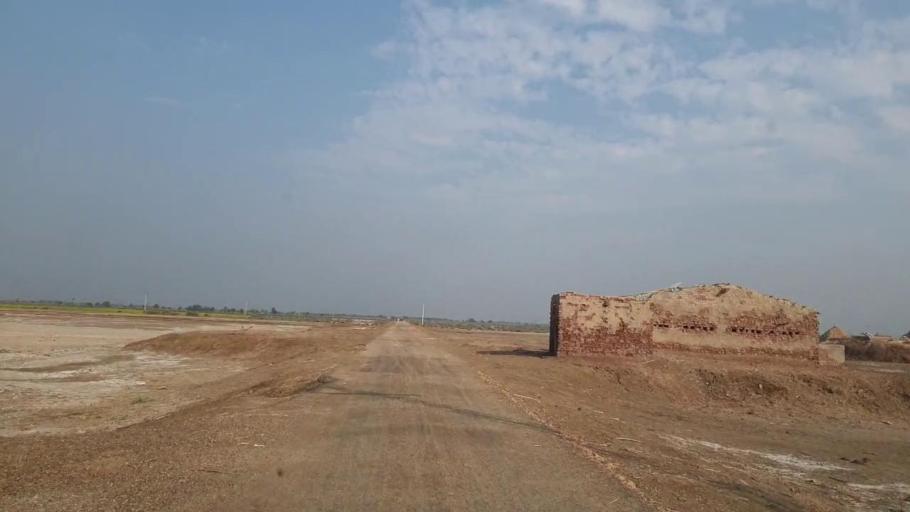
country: PK
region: Sindh
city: Mirpur Khas
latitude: 25.5629
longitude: 69.1891
